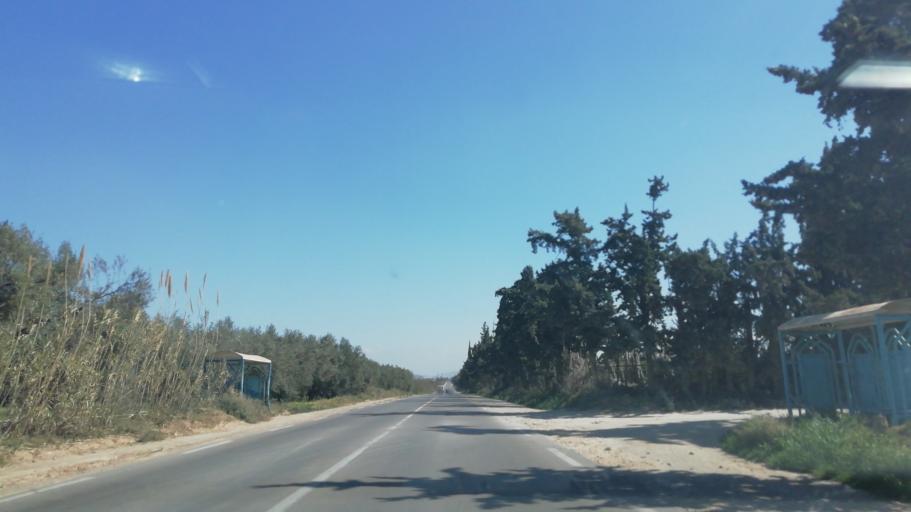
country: DZ
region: Mascara
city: Sig
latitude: 35.5681
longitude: -0.0604
